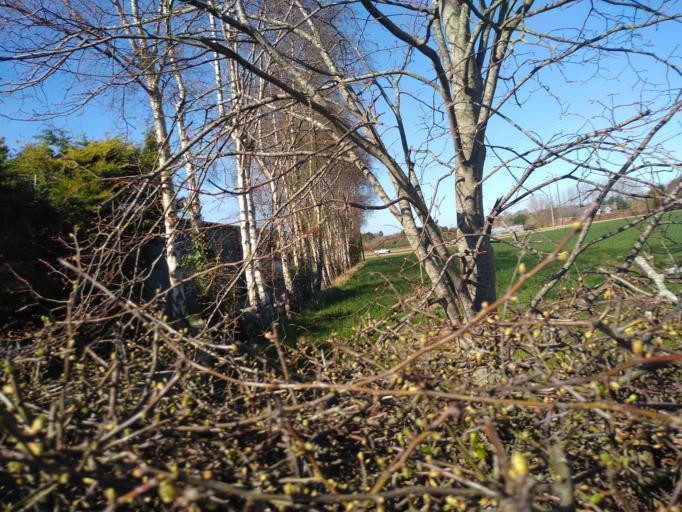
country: IE
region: Leinster
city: Malahide
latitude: 53.4371
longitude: -6.1666
